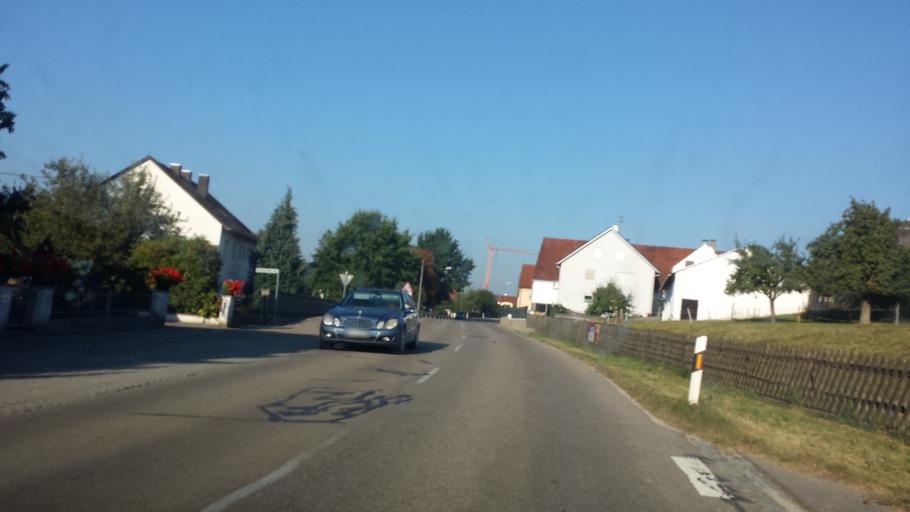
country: DE
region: Bavaria
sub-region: Upper Bavaria
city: Oberhausen
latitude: 48.7475
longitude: 11.1071
